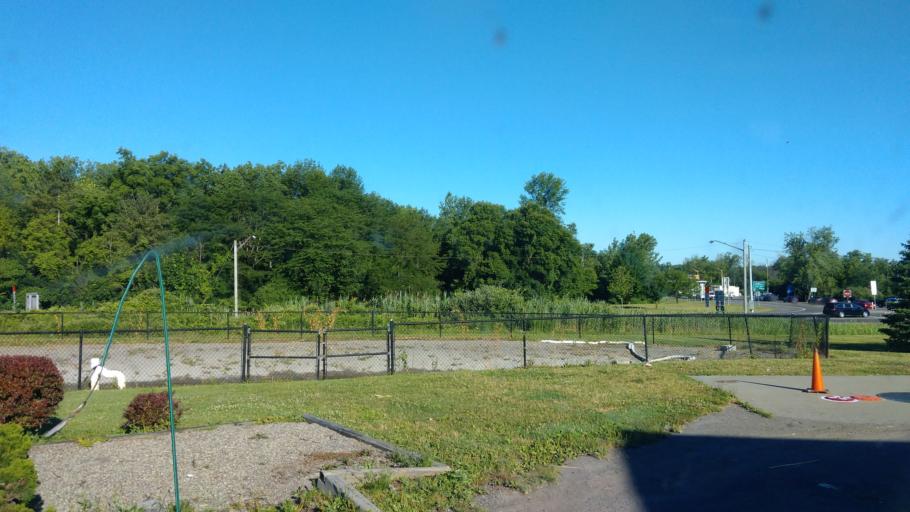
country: US
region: New York
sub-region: Ontario County
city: Phelps
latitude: 42.9511
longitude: -76.9766
